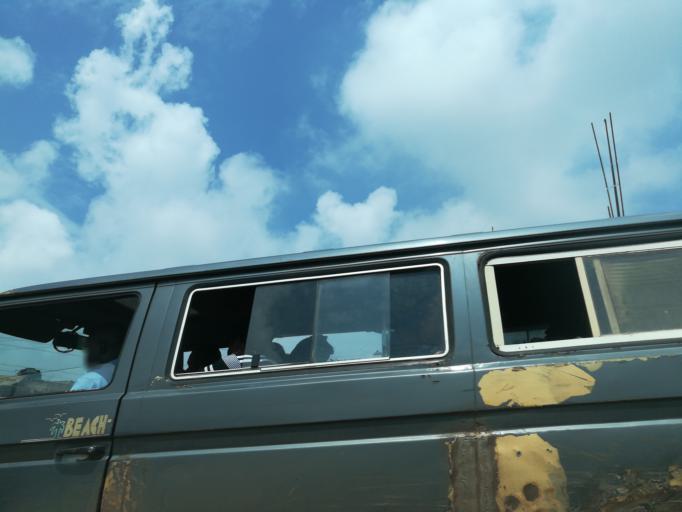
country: NG
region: Lagos
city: Ikorodu
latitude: 6.6795
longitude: 3.5115
